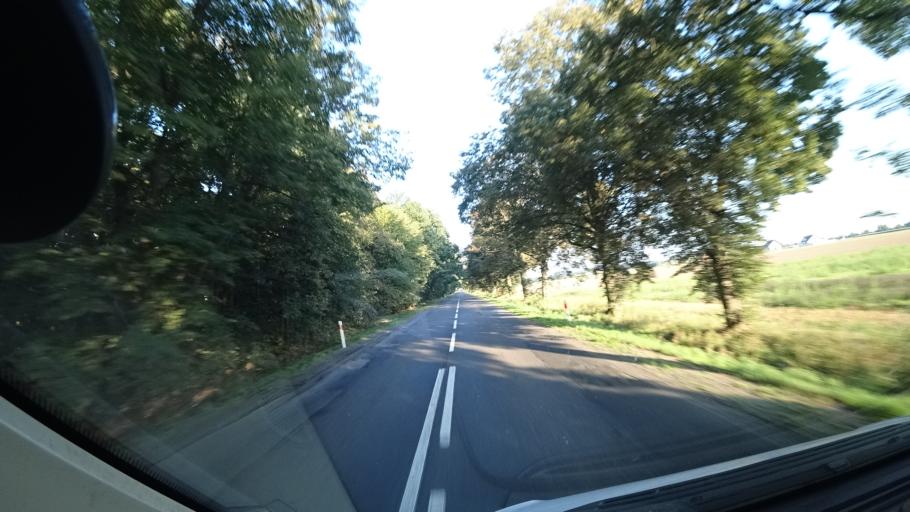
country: PL
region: Opole Voivodeship
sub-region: Powiat kedzierzynsko-kozielski
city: Bierawa
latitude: 50.2955
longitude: 18.2381
